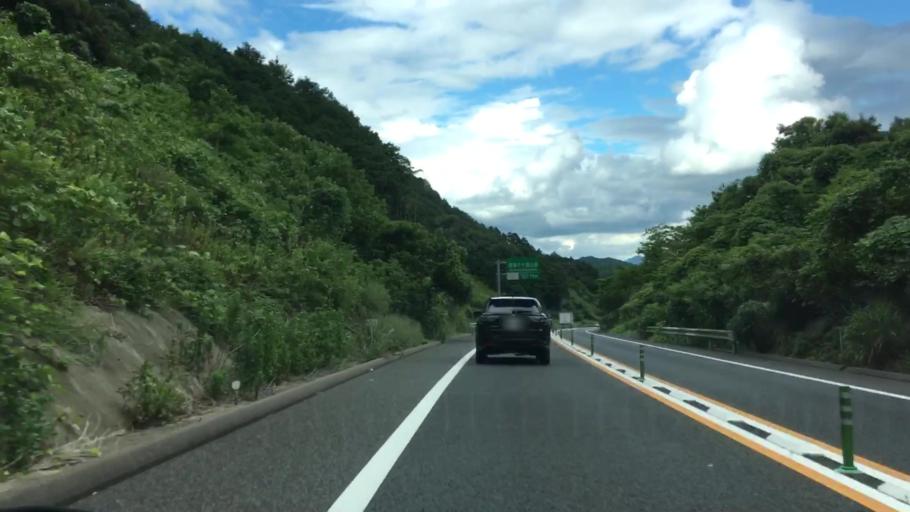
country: JP
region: Saga Prefecture
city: Karatsu
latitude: 33.4002
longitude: 129.9396
